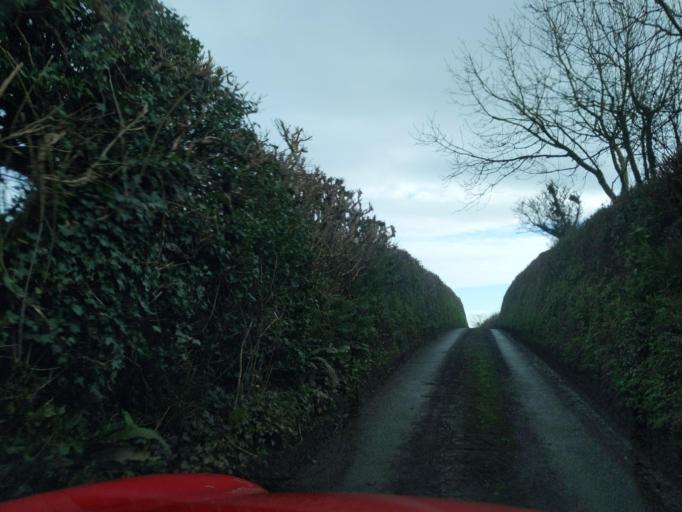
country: GB
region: England
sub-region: Devon
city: Salcombe
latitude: 50.2653
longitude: -3.6906
